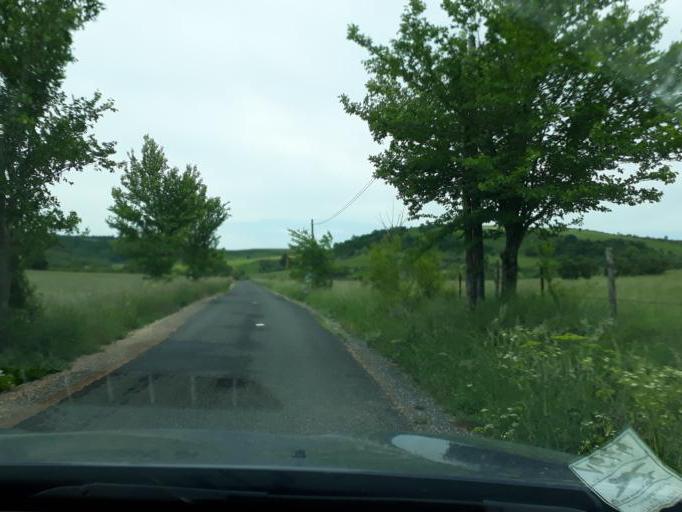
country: FR
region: Languedoc-Roussillon
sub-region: Departement de l'Herault
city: Lodeve
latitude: 43.8286
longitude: 3.2685
